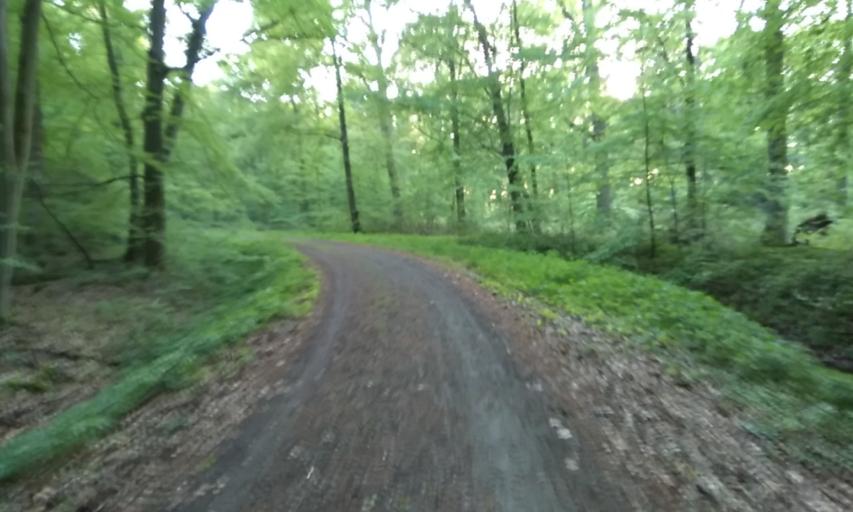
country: DE
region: Lower Saxony
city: Harsefeld
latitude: 53.4209
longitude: 9.4902
